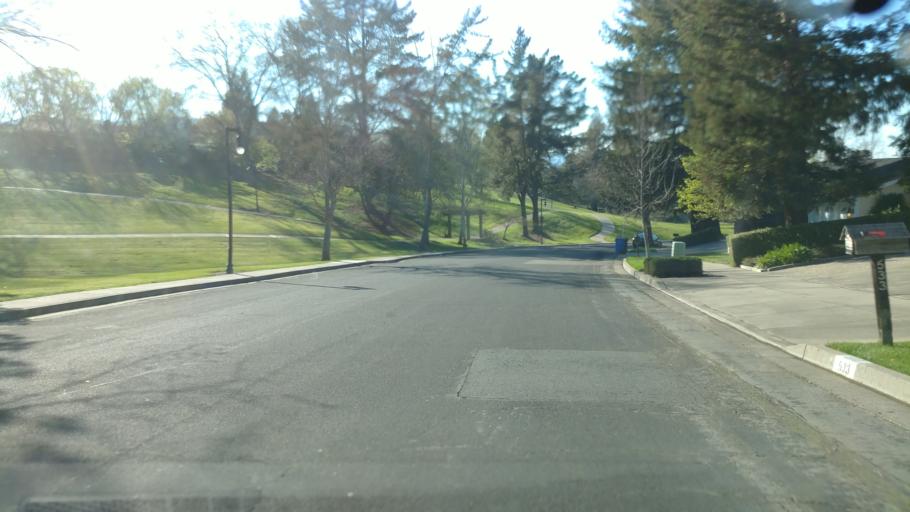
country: US
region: California
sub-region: Contra Costa County
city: Danville
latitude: 37.8197
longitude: -121.9832
